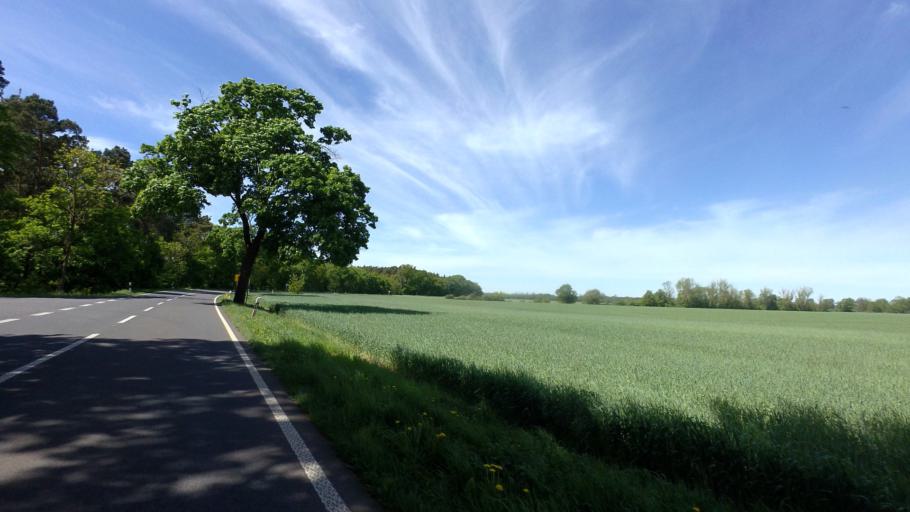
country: DE
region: Brandenburg
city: Baruth
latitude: 52.0664
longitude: 13.4714
